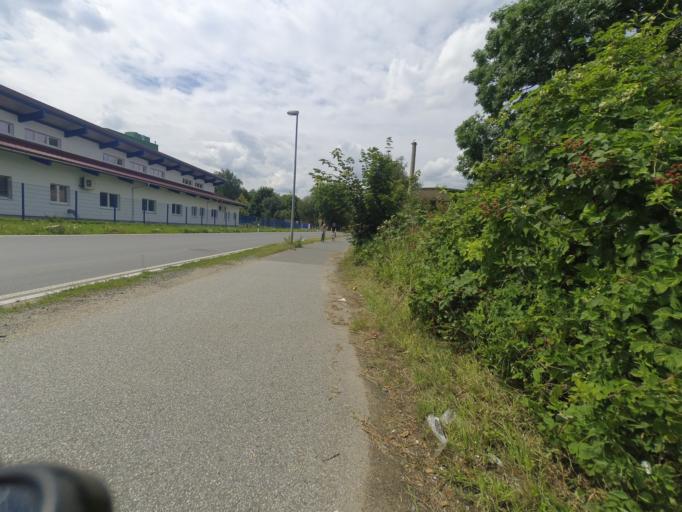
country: DE
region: Saxony
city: Heidenau
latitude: 50.9608
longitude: 13.8994
